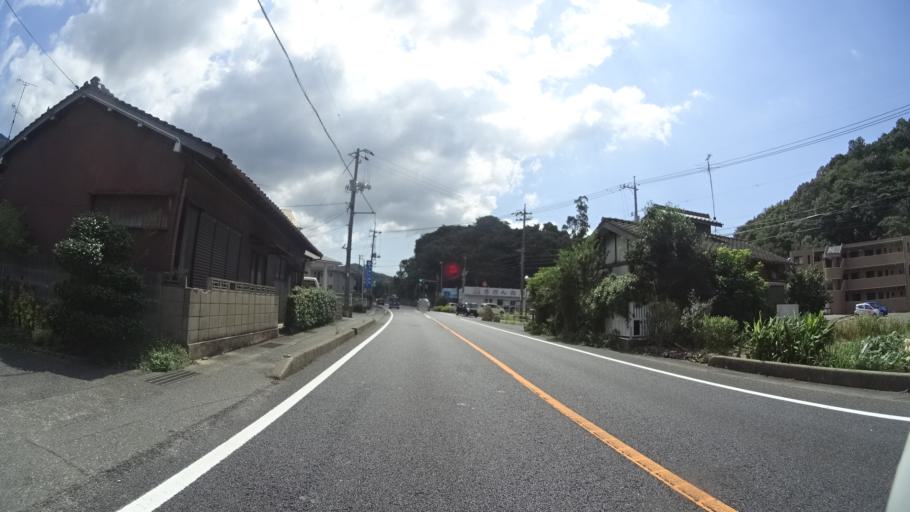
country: JP
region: Yamaguchi
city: Shimonoseki
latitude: 34.0667
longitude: 130.9053
